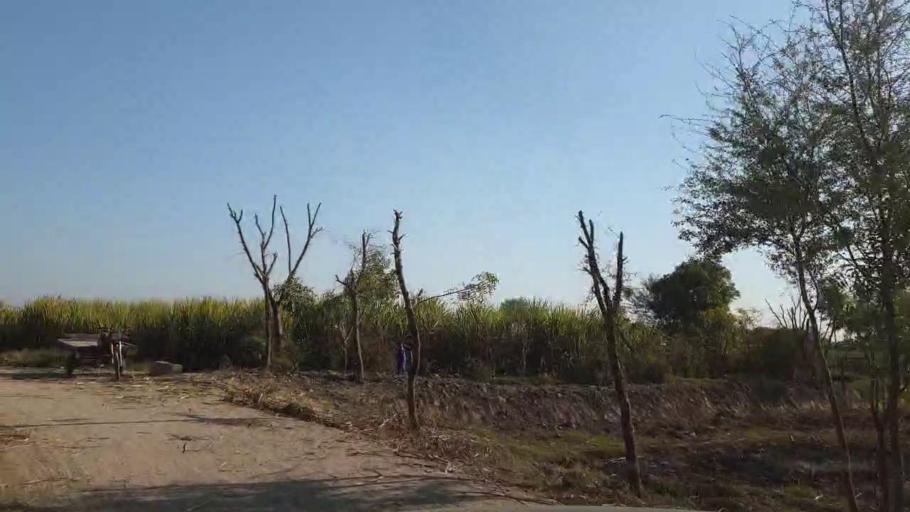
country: PK
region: Sindh
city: Tando Adam
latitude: 25.6856
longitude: 68.6881
